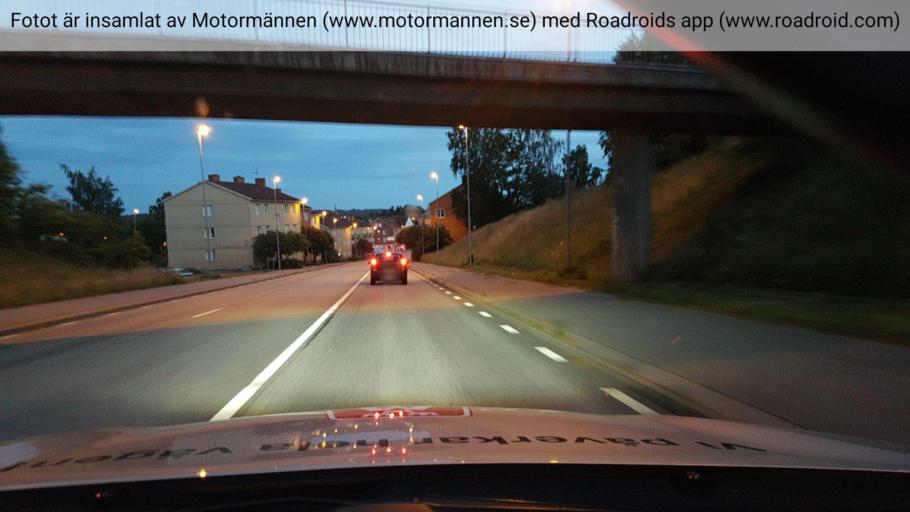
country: SE
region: OErebro
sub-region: Degerfors Kommun
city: Degerfors
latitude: 59.2400
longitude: 14.4343
